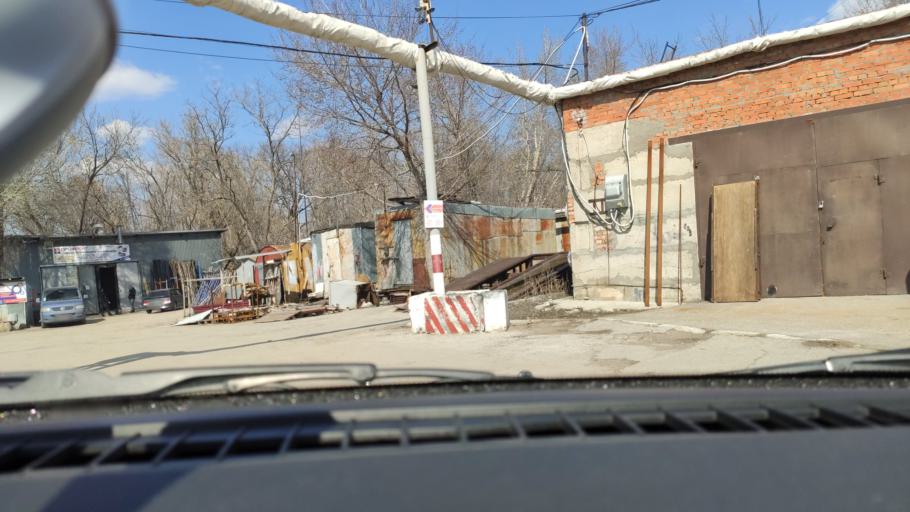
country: RU
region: Samara
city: Samara
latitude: 53.2703
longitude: 50.1889
